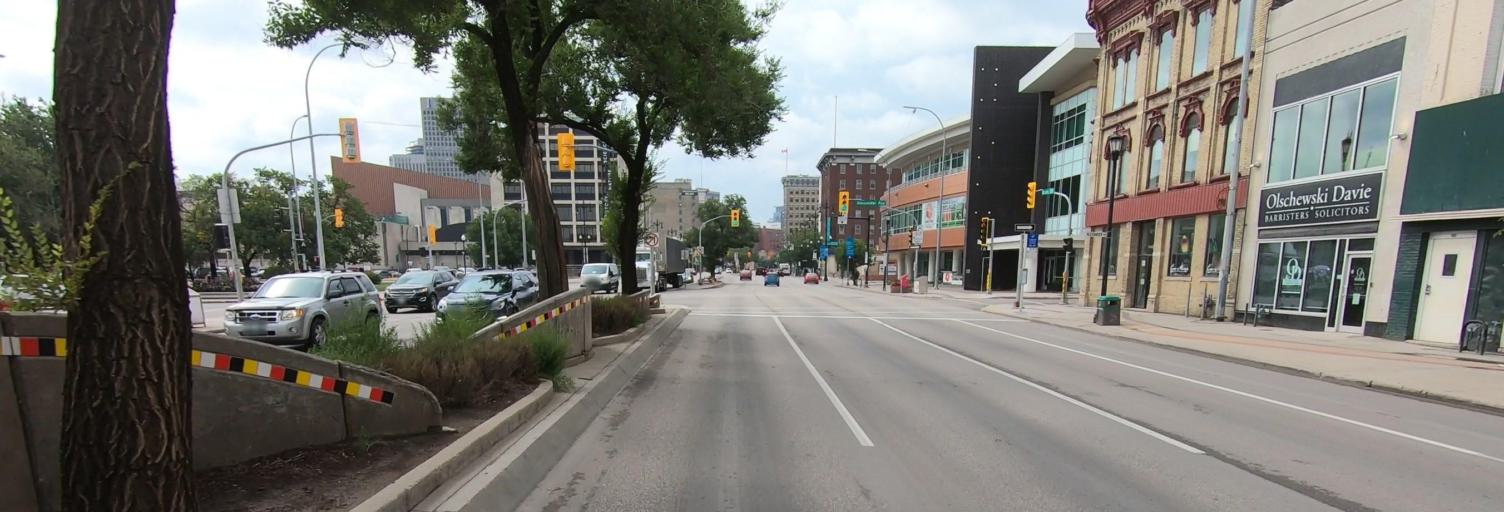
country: CA
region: Manitoba
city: Winnipeg
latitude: 49.9021
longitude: -97.1363
